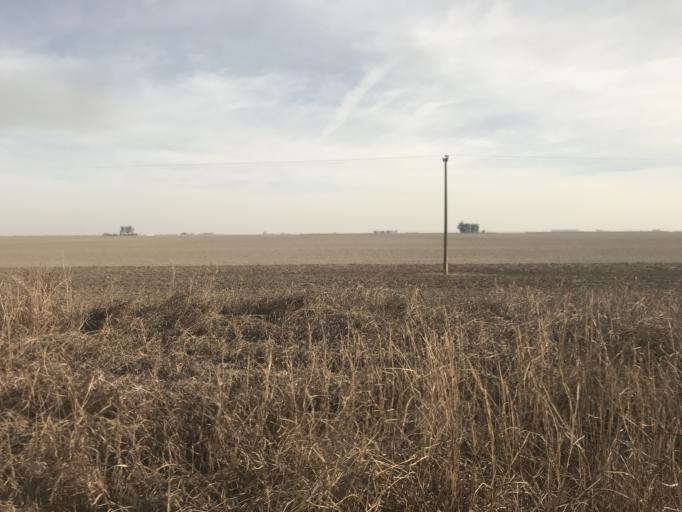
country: AR
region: Cordoba
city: Laguna Larga
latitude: -31.7340
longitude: -63.8406
